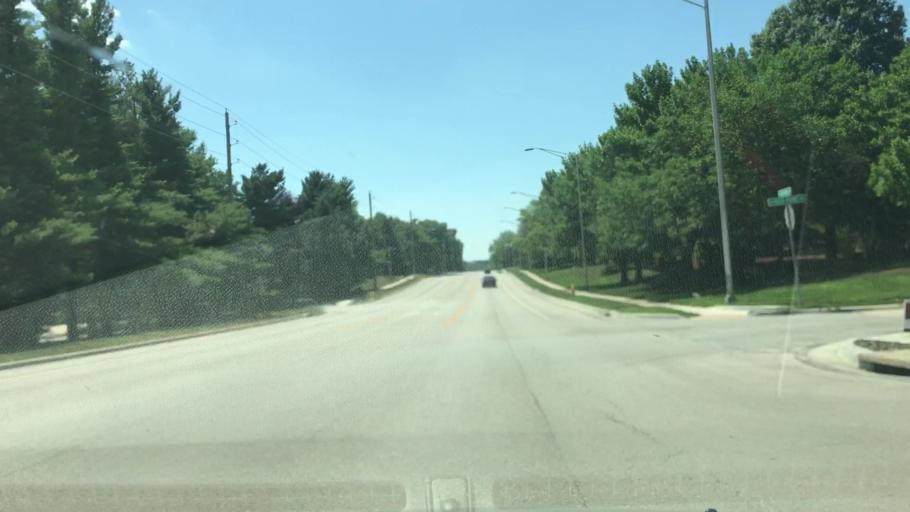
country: US
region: Missouri
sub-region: Jackson County
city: Lees Summit
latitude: 38.9268
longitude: -94.4231
